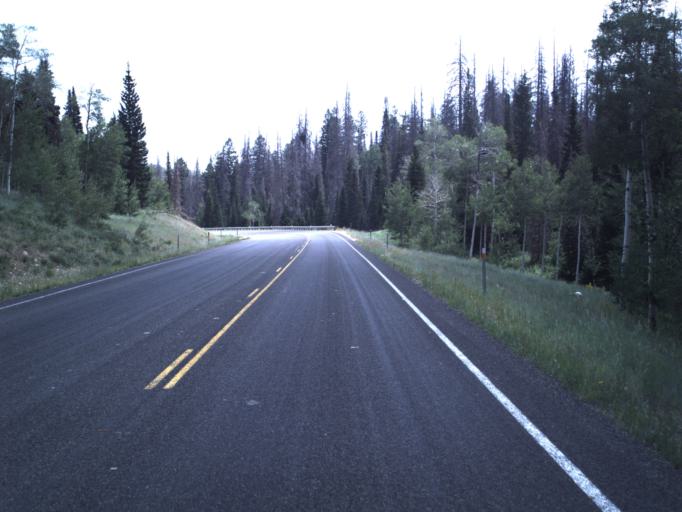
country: US
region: Utah
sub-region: Summit County
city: Francis
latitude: 40.4838
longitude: -110.9504
